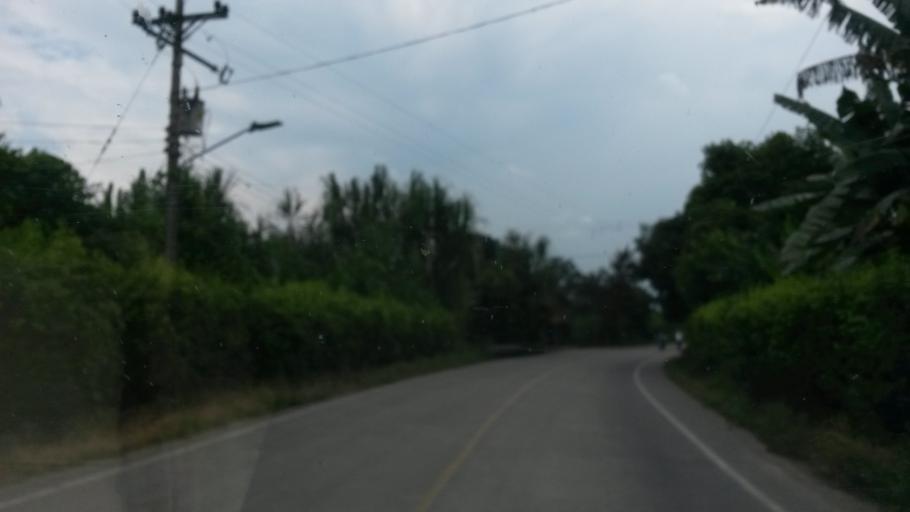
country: CO
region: Cauca
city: Padilla
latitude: 3.2306
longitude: -76.3242
